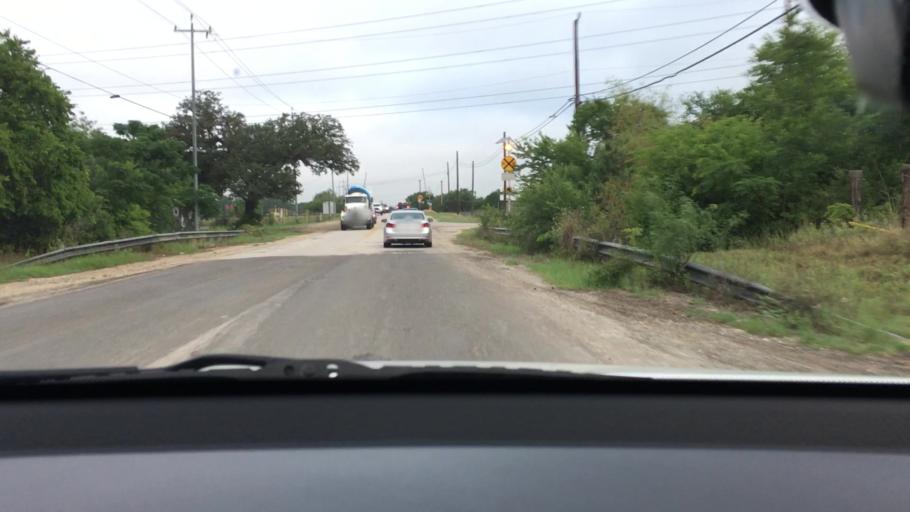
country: US
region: Texas
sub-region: Bexar County
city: Selma
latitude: 29.6064
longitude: -98.3299
